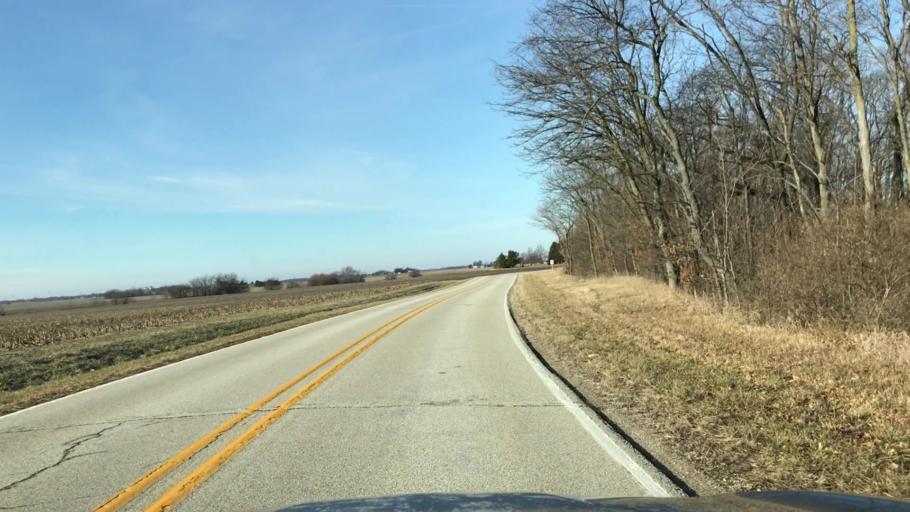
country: US
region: Illinois
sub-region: McLean County
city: Hudson
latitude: 40.6261
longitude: -88.9297
